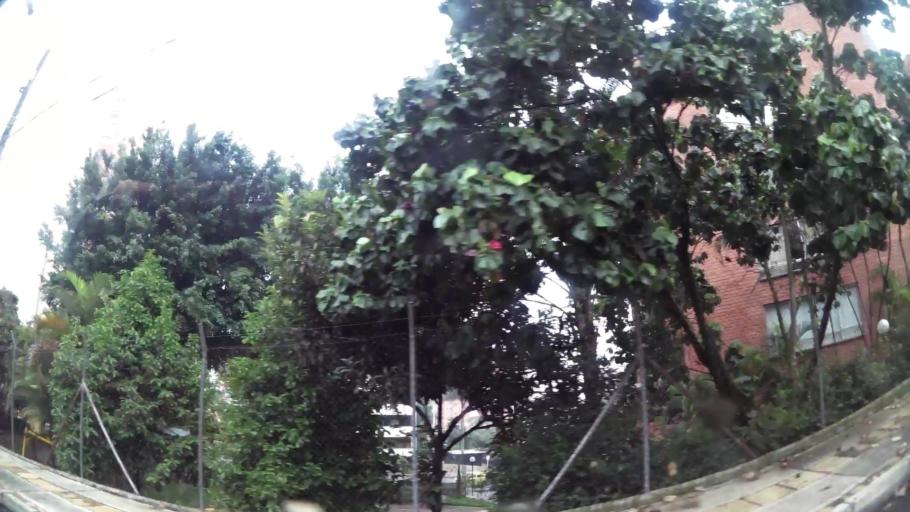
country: CO
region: Antioquia
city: Envigado
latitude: 6.1924
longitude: -75.5667
